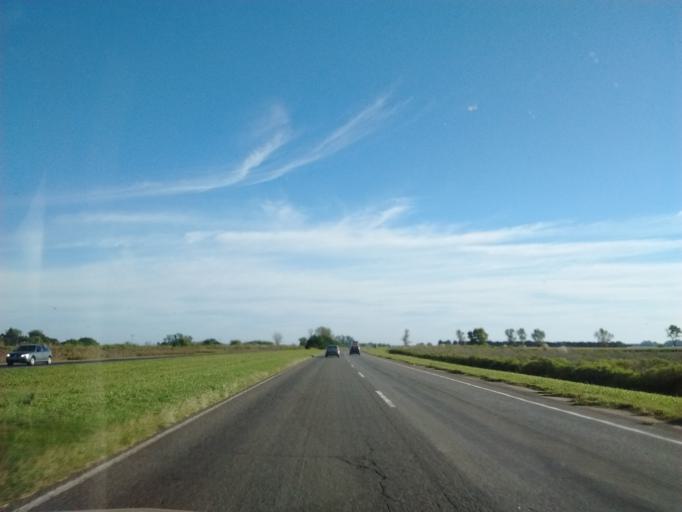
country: AR
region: Santa Fe
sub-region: Departamento de San Lorenzo
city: San Lorenzo
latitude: -32.5668
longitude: -60.8813
